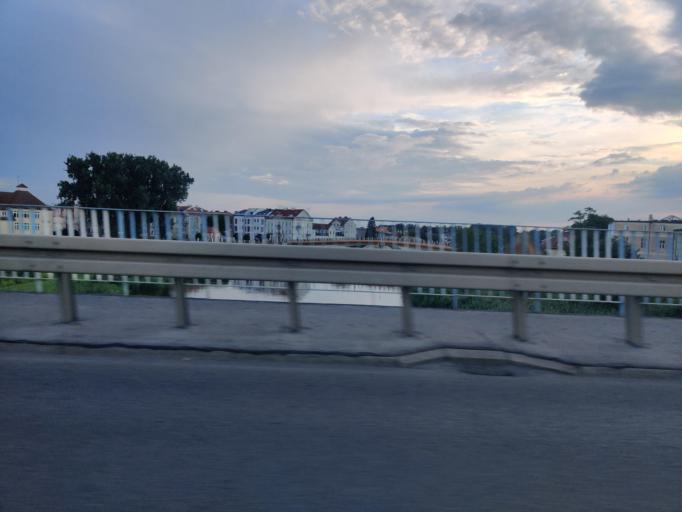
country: PL
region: Greater Poland Voivodeship
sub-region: Konin
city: Konin
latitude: 52.2143
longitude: 18.2572
